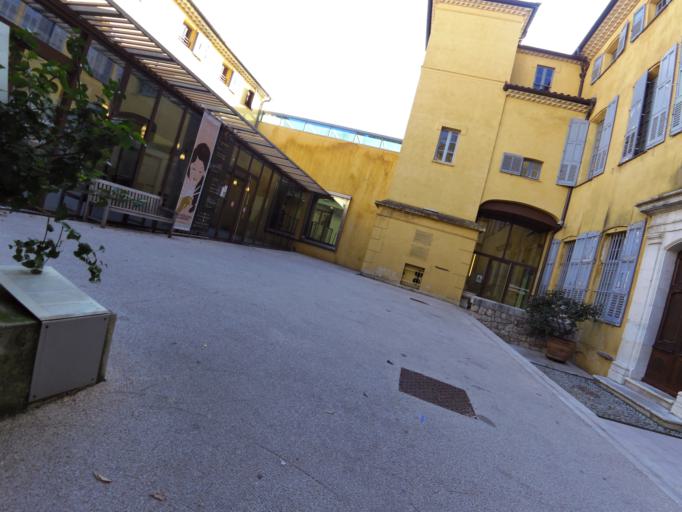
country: FR
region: Provence-Alpes-Cote d'Azur
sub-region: Departement des Alpes-Maritimes
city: Grasse
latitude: 43.6582
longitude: 6.9218
